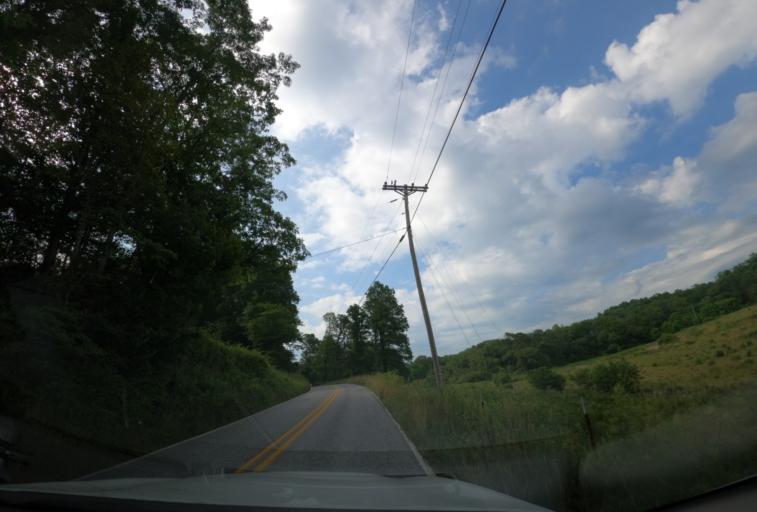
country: US
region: Georgia
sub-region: Rabun County
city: Mountain City
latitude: 34.9975
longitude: -83.2982
